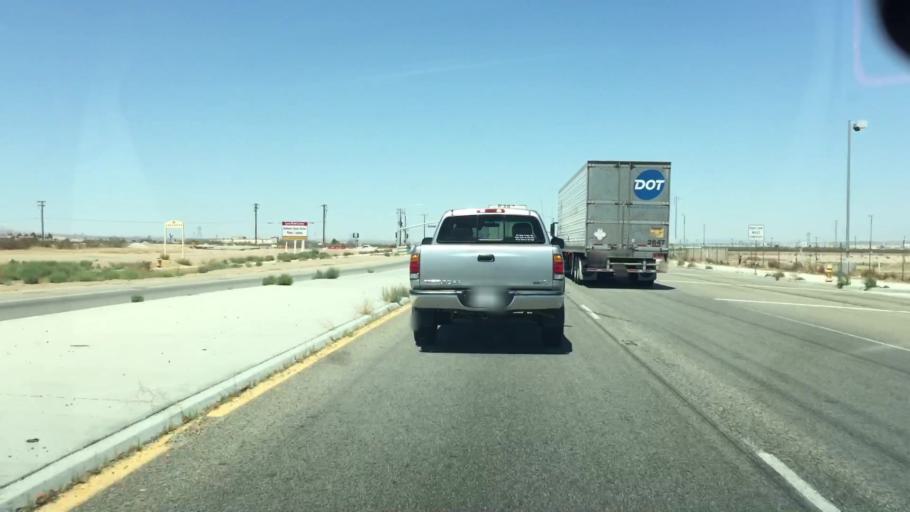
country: US
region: California
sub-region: San Bernardino County
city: Adelanto
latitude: 34.5265
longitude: -117.3994
